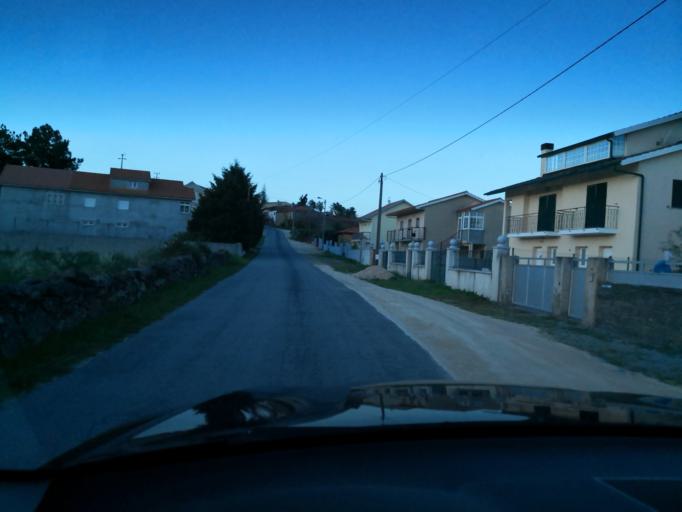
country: PT
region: Vila Real
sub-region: Vila Real
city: Vila Real
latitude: 41.3480
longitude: -7.6870
